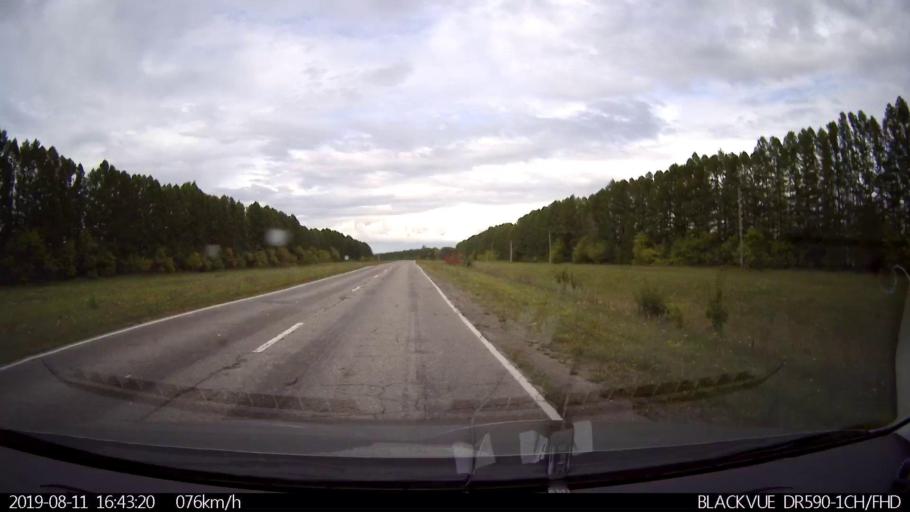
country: RU
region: Ulyanovsk
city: Mayna
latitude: 54.1680
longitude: 47.6710
